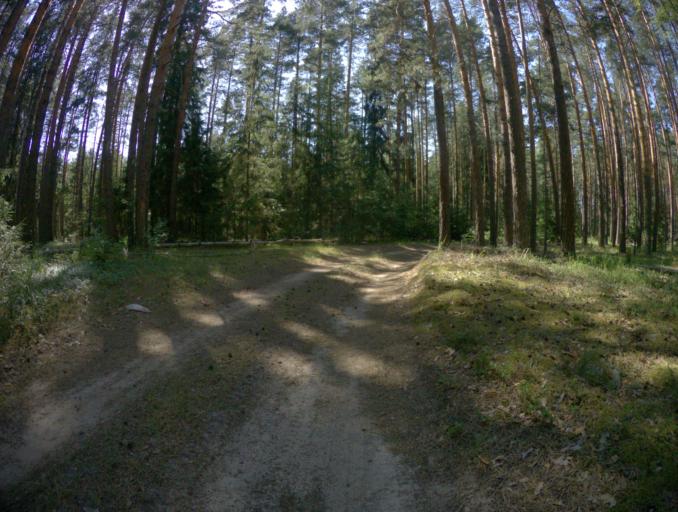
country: RU
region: Vladimir
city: Vyazniki
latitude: 56.3842
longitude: 42.2238
